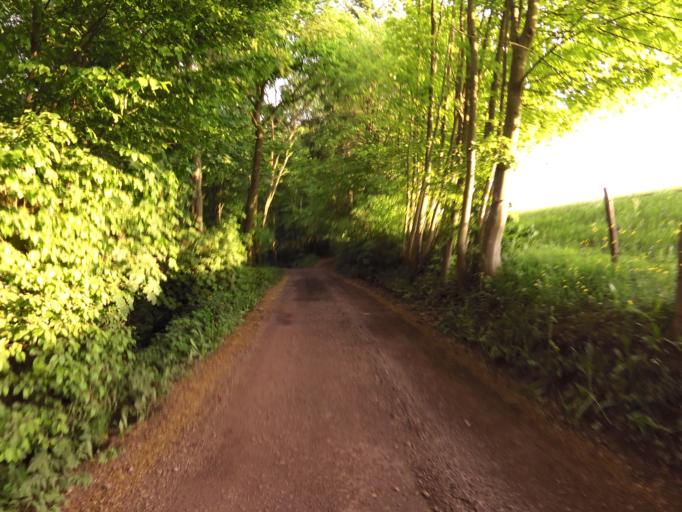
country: DE
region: Thuringia
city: Frauensee
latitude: 50.9044
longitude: 10.1073
